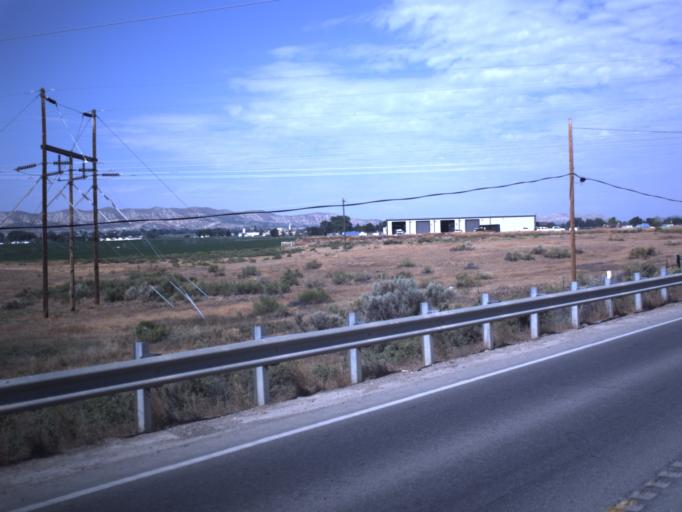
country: US
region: Utah
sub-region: Uintah County
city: Naples
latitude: 40.3991
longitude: -109.4637
